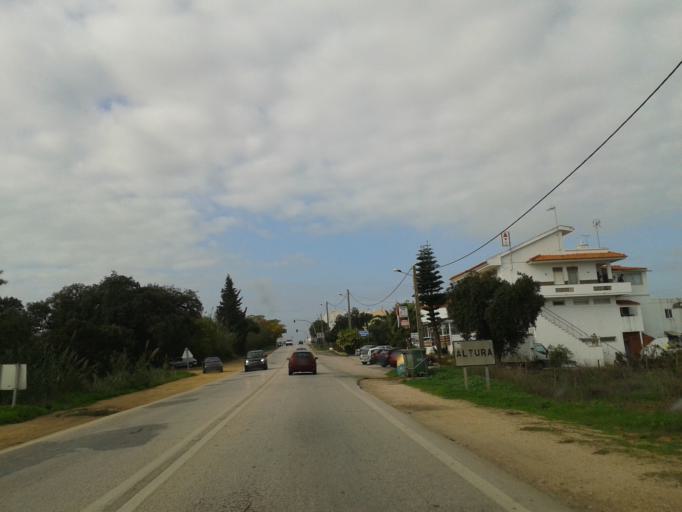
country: PT
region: Faro
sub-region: Vila Real de Santo Antonio
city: Monte Gordo
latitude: 37.1811
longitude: -7.4996
